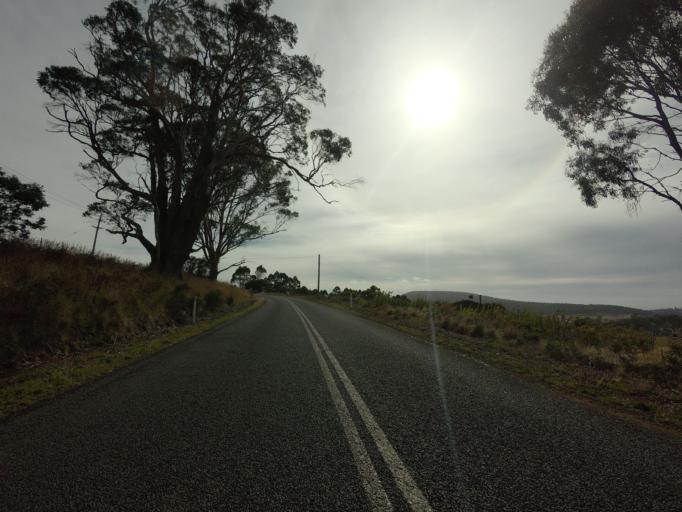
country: AU
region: Tasmania
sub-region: Brighton
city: Bridgewater
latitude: -42.3830
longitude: 147.4237
